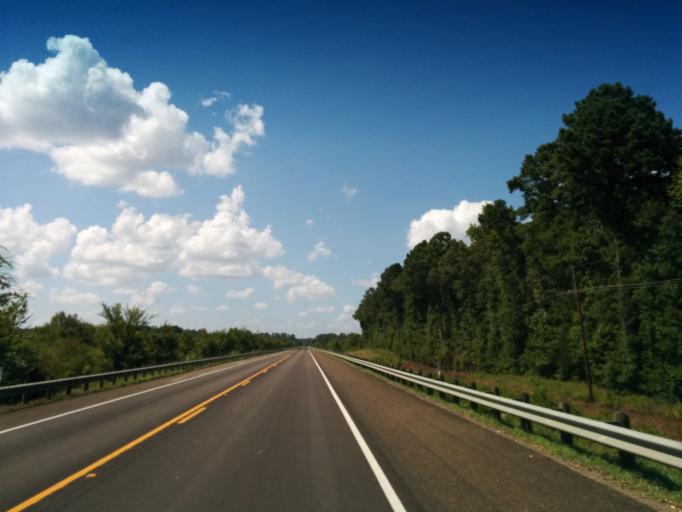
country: US
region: Texas
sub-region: Jasper County
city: Sam Rayburn
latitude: 31.1728
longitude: -93.9717
